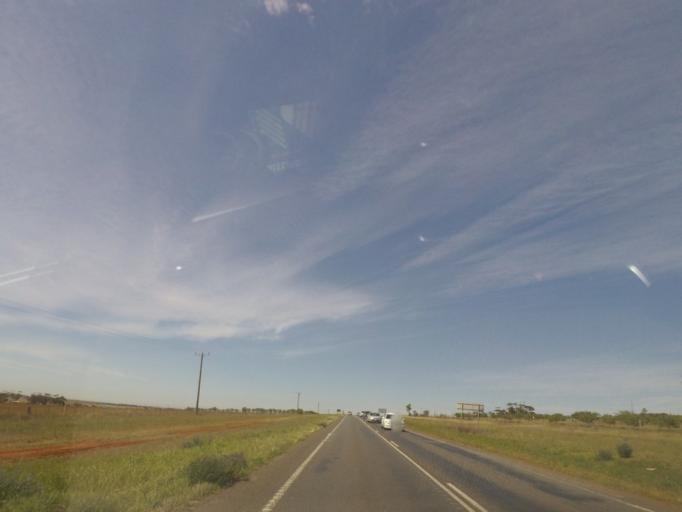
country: AU
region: Victoria
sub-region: Moorabool
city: Bacchus Marsh
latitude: -37.7710
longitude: 144.4391
